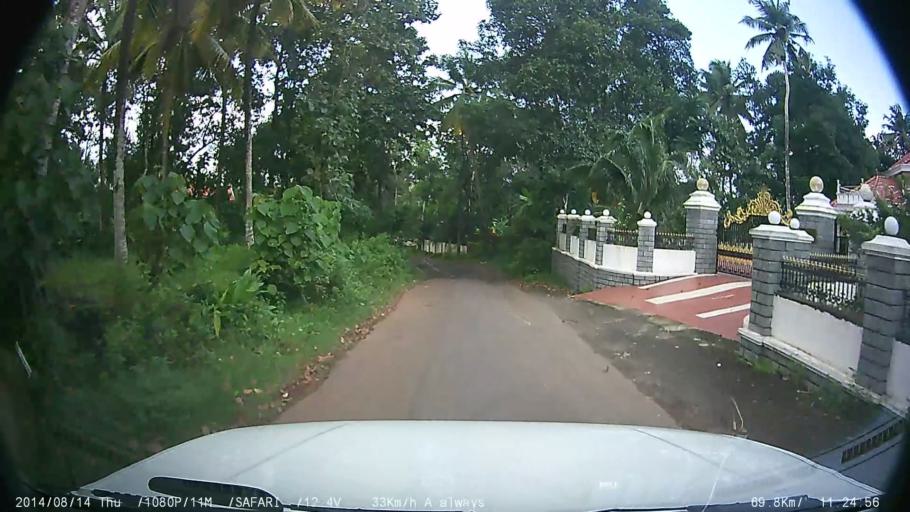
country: IN
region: Kerala
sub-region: Kottayam
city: Kottayam
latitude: 9.5341
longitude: 76.5331
